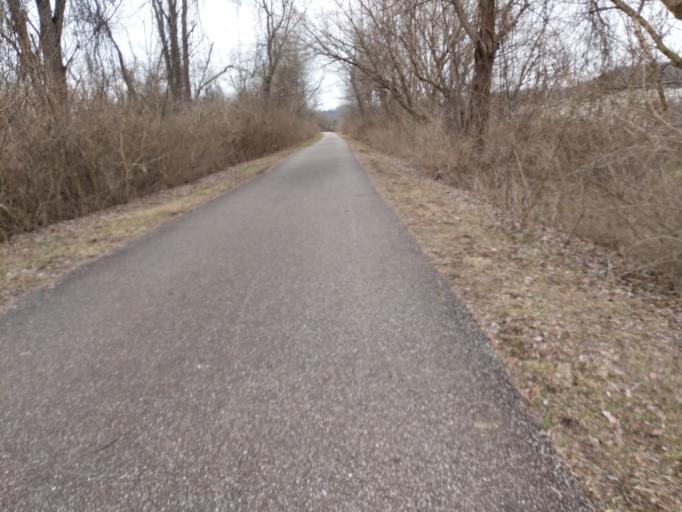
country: US
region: Ohio
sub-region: Athens County
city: Athens
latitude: 39.3349
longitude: -82.0707
